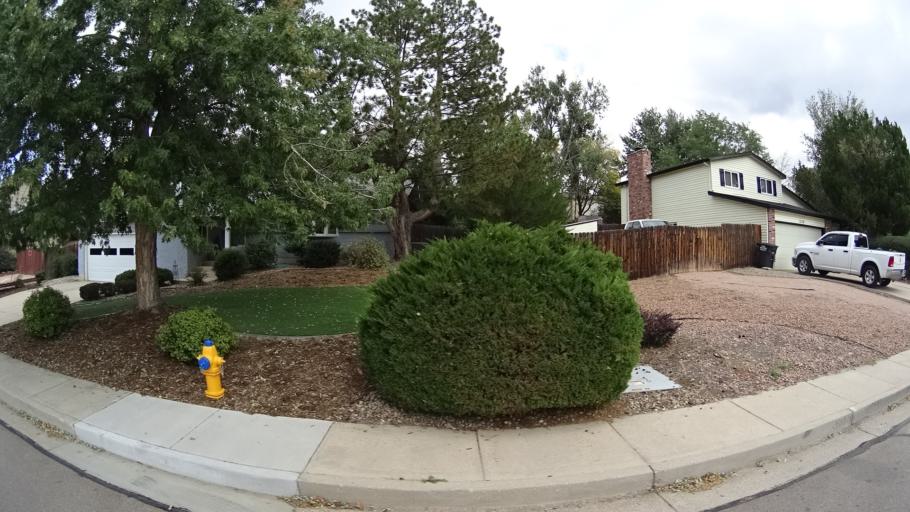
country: US
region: Colorado
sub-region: El Paso County
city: Cimarron Hills
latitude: 38.8837
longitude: -104.7323
